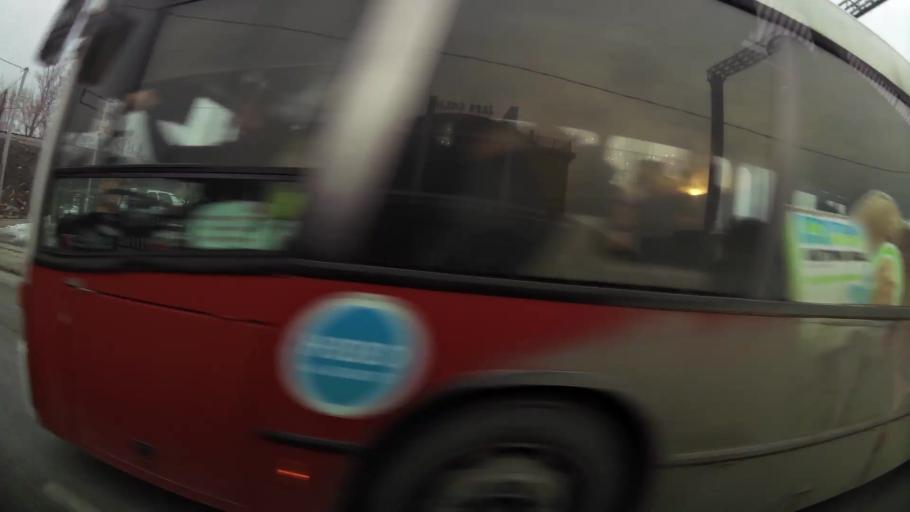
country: MK
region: Suto Orizari
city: Suto Orizare
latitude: 42.0271
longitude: 21.4294
